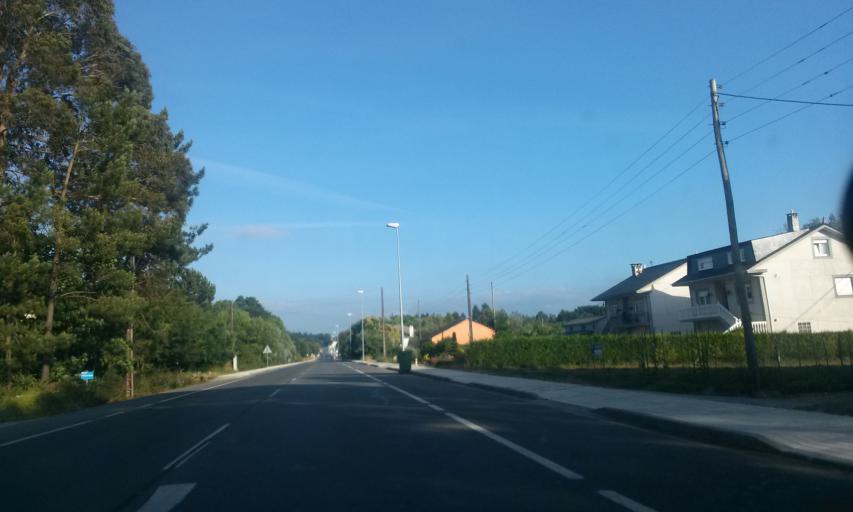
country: ES
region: Galicia
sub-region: Provincia de Lugo
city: Begonte
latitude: 43.1569
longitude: -7.6940
